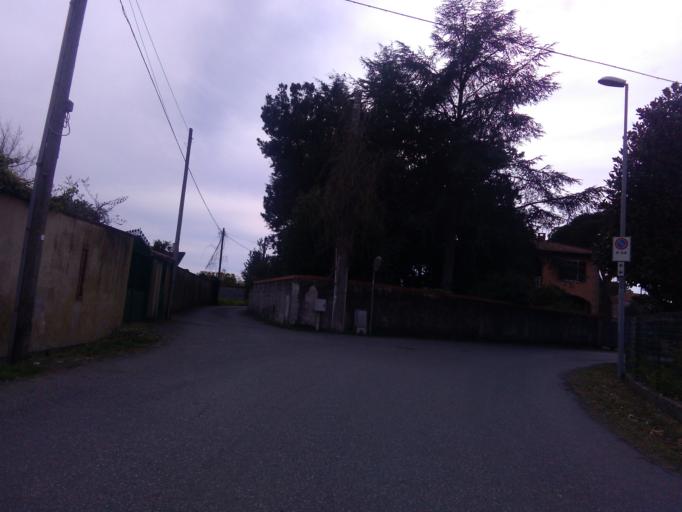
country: IT
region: Tuscany
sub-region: Provincia di Massa-Carrara
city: Marina di Carrara
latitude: 44.0521
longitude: 10.0432
